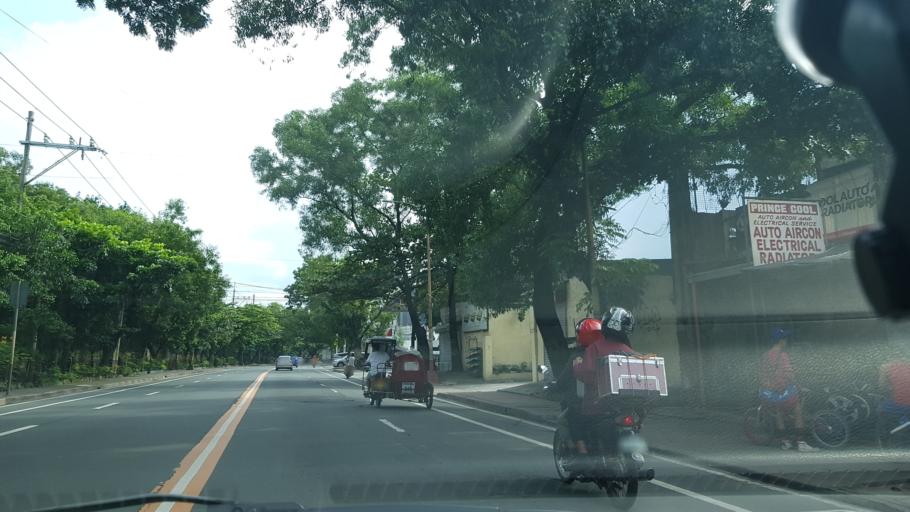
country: PH
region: Metro Manila
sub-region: Pasig
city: Pasig City
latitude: 14.5810
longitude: 121.0871
